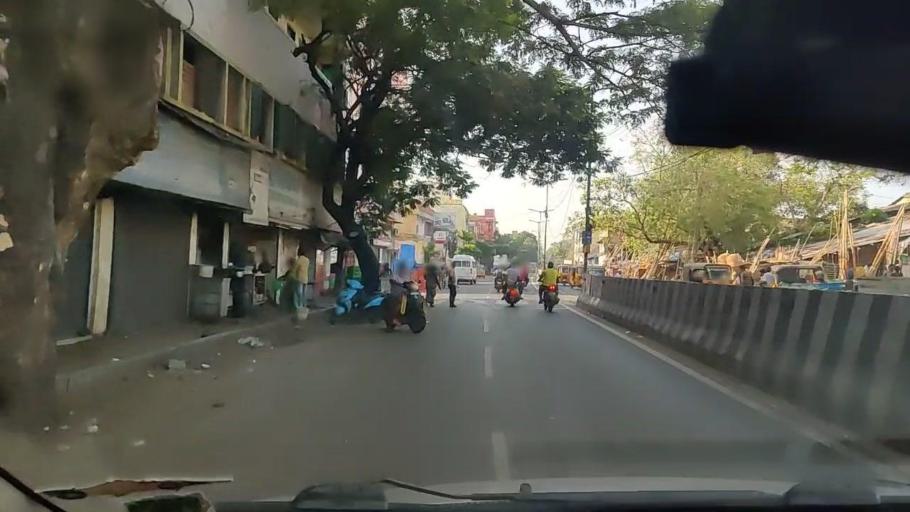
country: IN
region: Tamil Nadu
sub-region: Chennai
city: George Town
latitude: 13.0997
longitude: 80.2752
